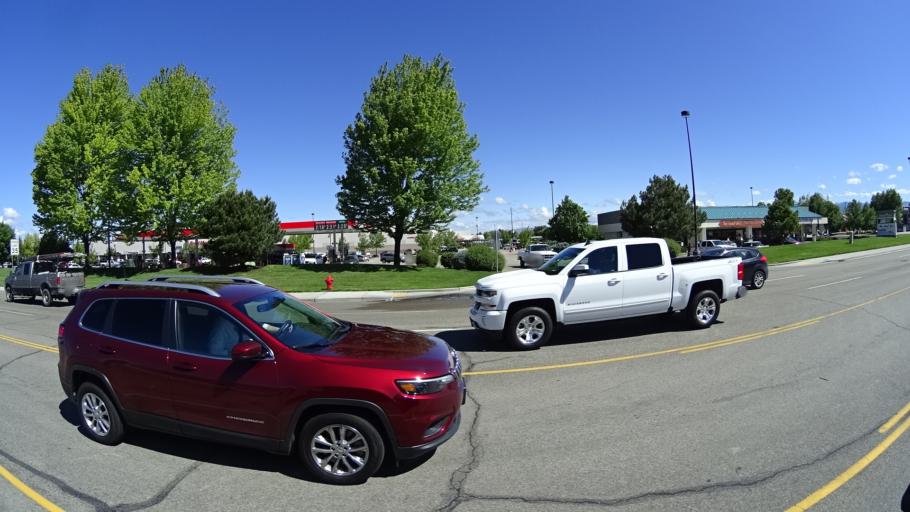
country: US
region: Idaho
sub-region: Ada County
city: Meridian
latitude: 43.6194
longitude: -116.3715
